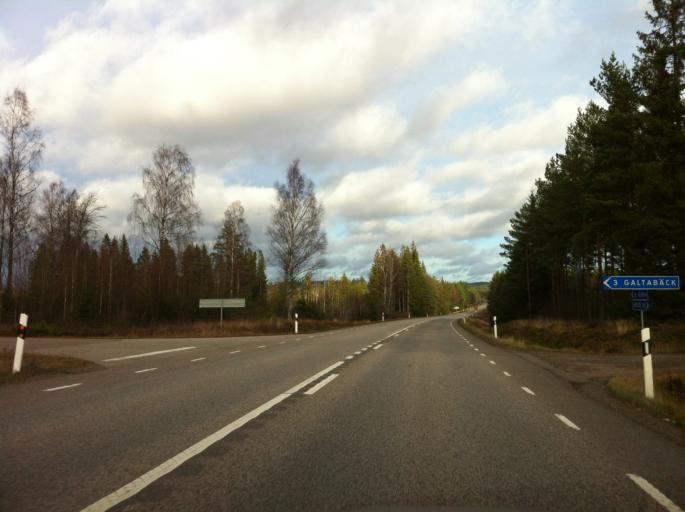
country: SE
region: Kronoberg
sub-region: Vaxjo Kommun
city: Braas
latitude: 57.0734
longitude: 15.1657
